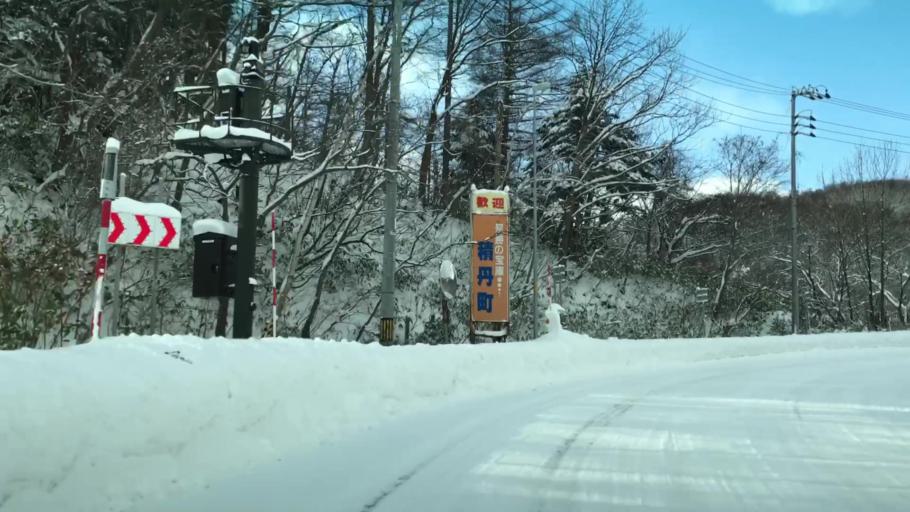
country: JP
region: Hokkaido
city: Yoichi
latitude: 43.2908
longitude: 140.5898
